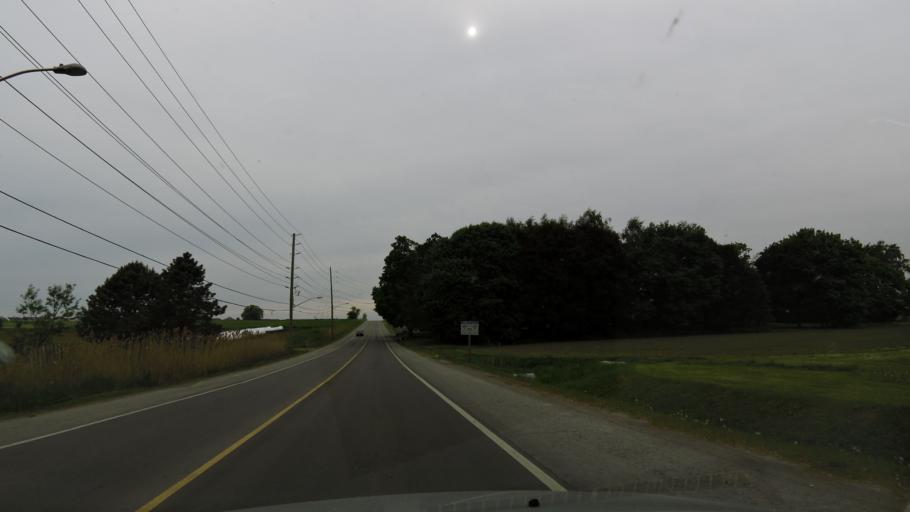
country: CA
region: Ontario
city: Ajax
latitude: 43.8868
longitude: -78.9967
